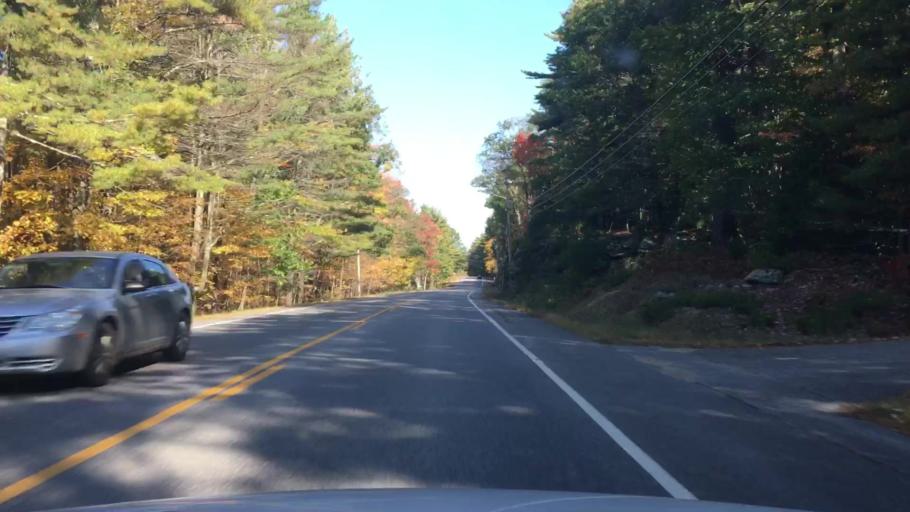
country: US
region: Maine
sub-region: Sagadahoc County
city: Topsham
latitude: 44.0009
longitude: -69.9502
